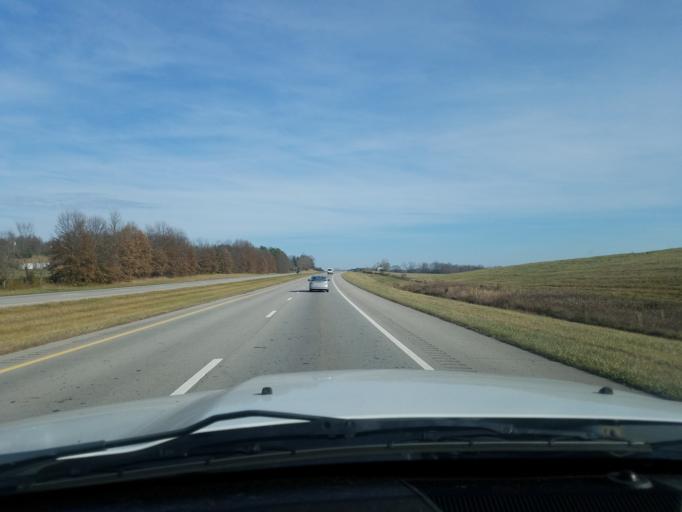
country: US
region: Ohio
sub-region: Athens County
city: Athens
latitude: 39.2199
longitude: -82.2141
